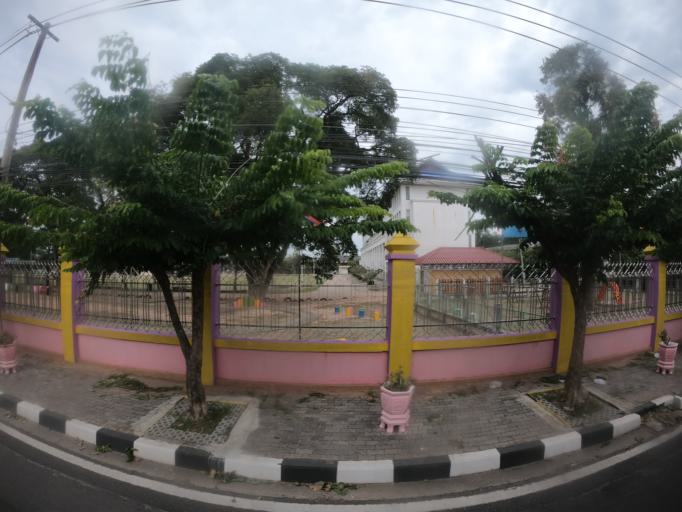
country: TH
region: Maha Sarakham
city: Maha Sarakham
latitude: 16.1884
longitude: 103.2984
